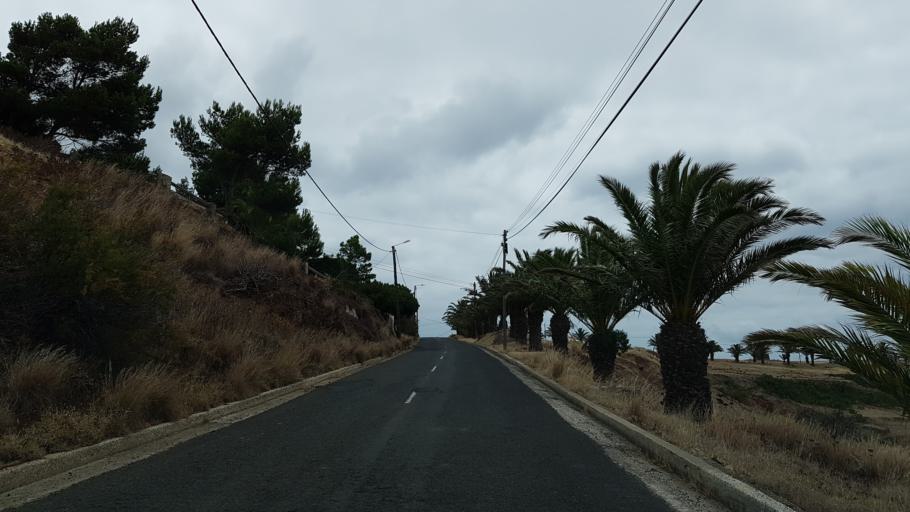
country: PT
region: Madeira
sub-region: Porto Santo
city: Vila de Porto Santo
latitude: 33.0688
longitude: -16.3198
